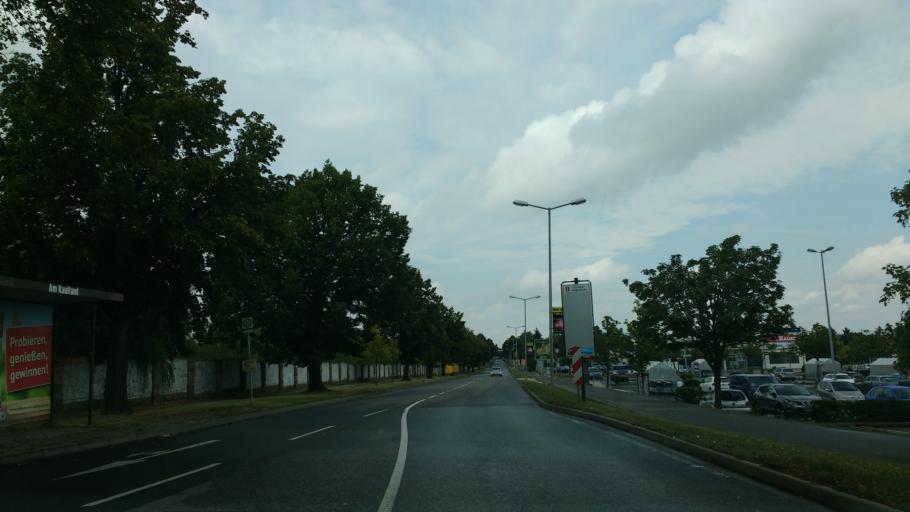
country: DE
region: Saxony-Anhalt
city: Zeitz
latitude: 51.0361
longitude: 12.1278
